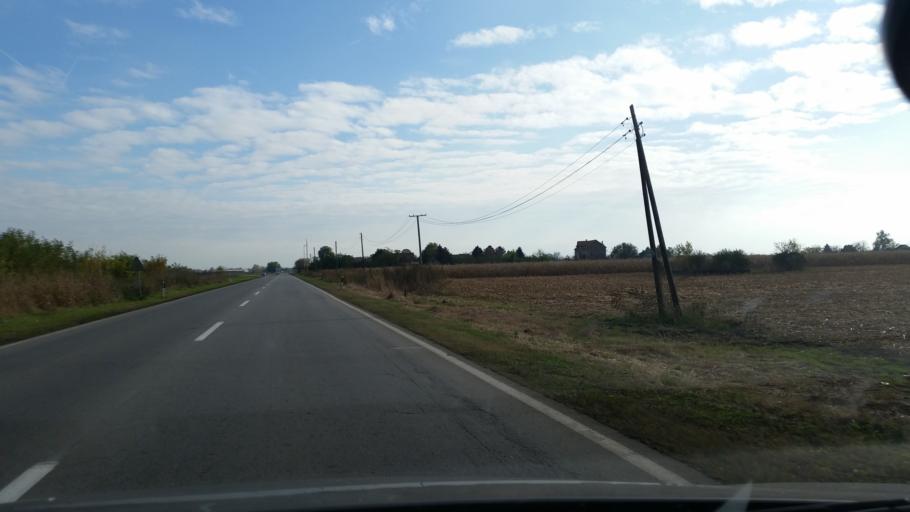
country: RS
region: Autonomna Pokrajina Vojvodina
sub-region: Srednjebanatski Okrug
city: Zrenjanin
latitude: 45.4107
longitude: 20.3736
